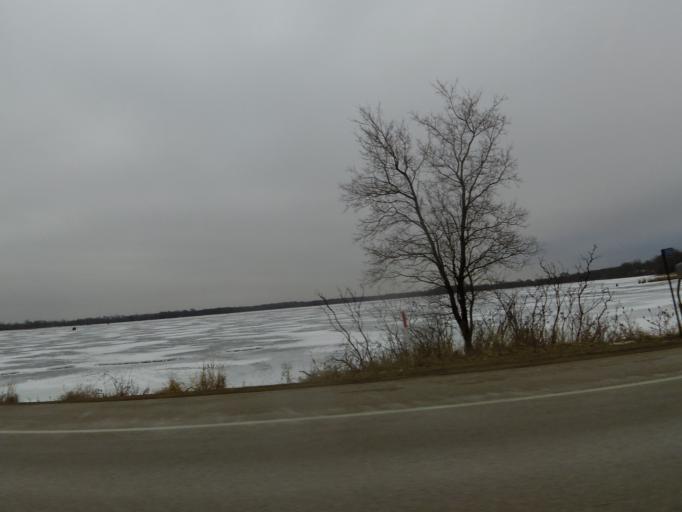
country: US
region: Minnesota
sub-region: Carver County
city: Watertown
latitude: 44.9322
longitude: -93.8309
